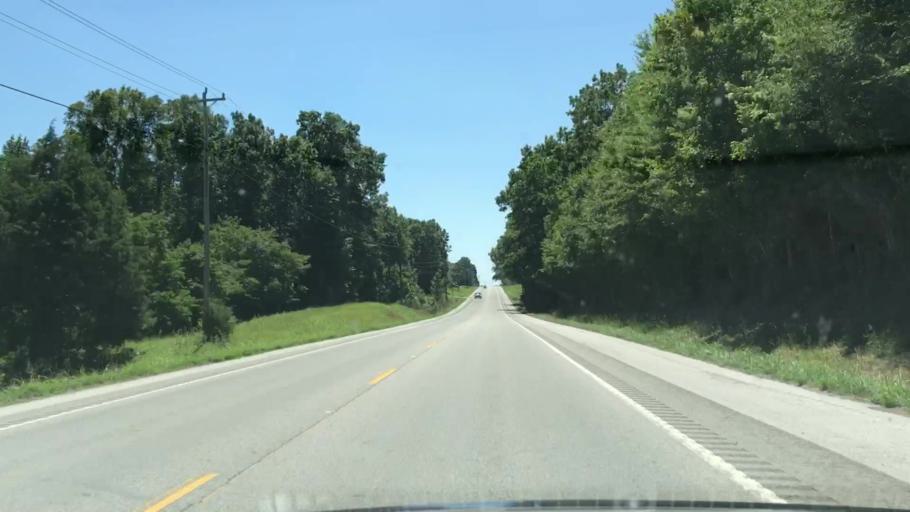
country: US
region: Tennessee
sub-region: Jackson County
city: Dodson Branch
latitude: 36.2546
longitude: -85.6124
